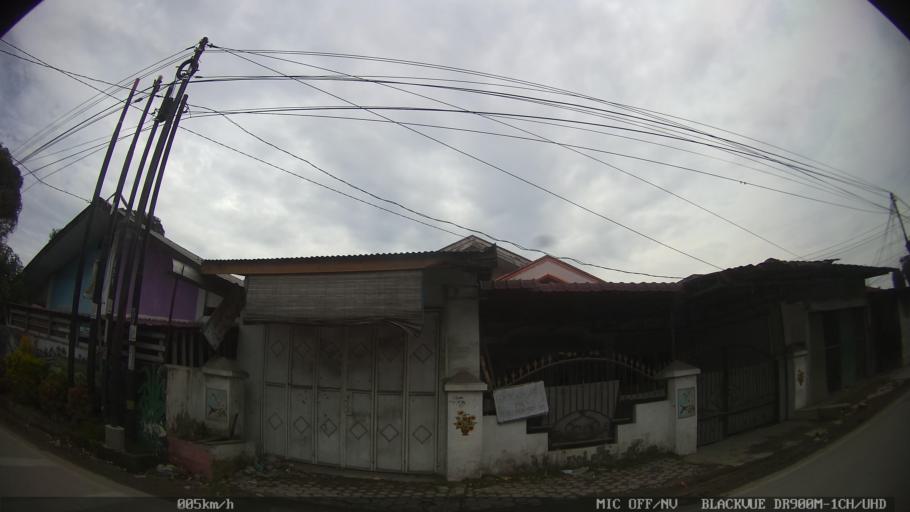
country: ID
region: North Sumatra
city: Sunggal
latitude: 3.6120
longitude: 98.6060
